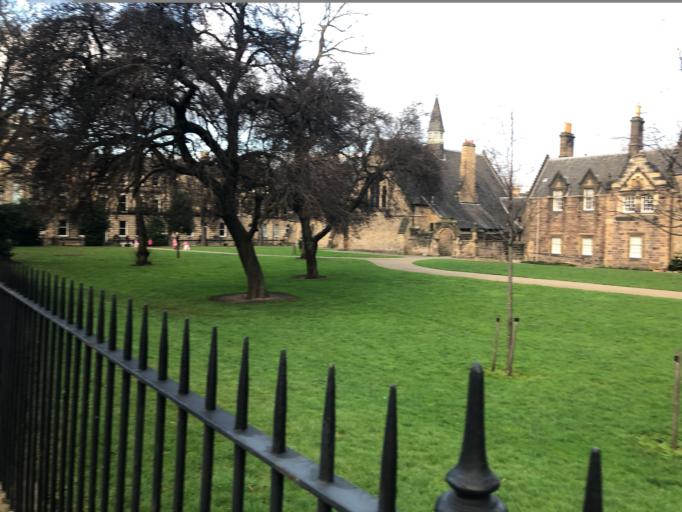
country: GB
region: Scotland
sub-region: Edinburgh
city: Edinburgh
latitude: 55.9485
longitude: -3.2171
